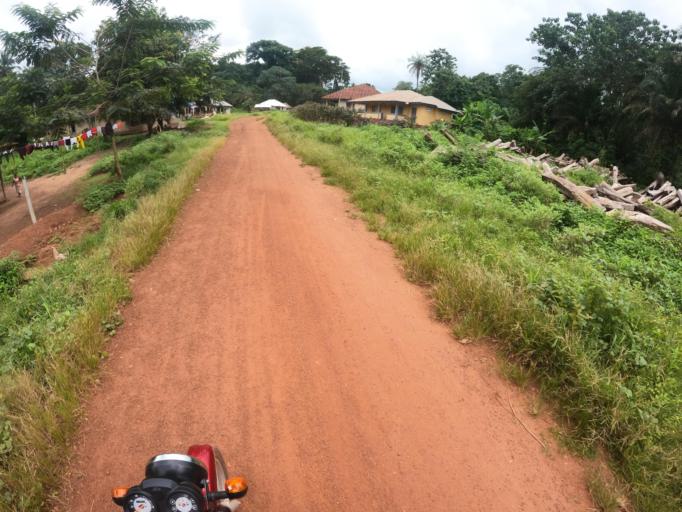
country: SL
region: Northern Province
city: Kamakwie
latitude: 9.5092
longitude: -12.2660
